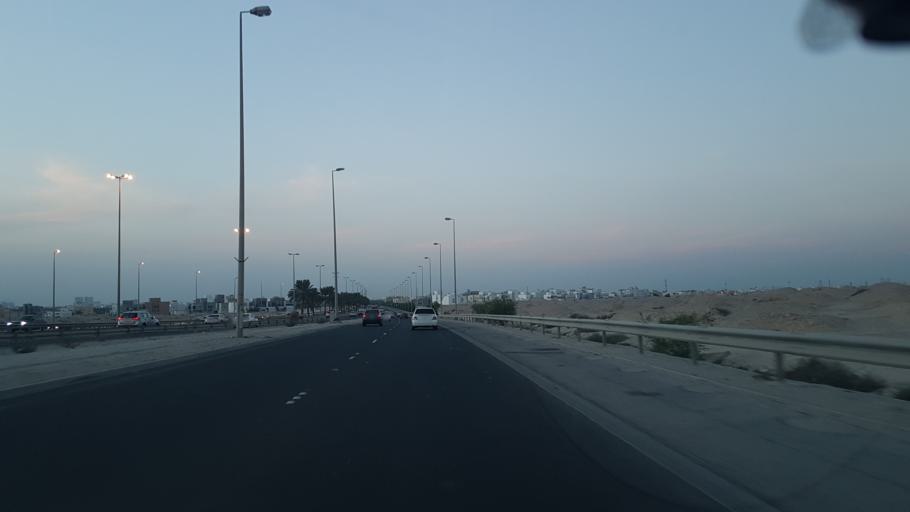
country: BH
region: Central Governorate
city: Madinat Hamad
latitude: 26.1442
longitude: 50.5105
